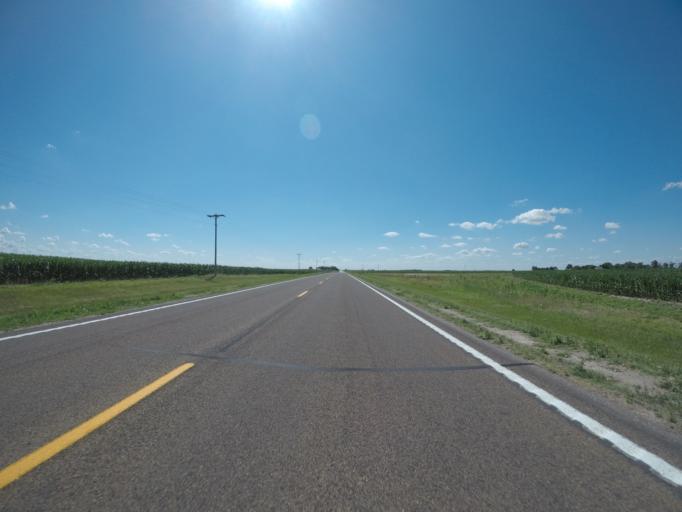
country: US
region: Nebraska
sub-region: Chase County
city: Imperial
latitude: 40.5377
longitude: -101.7195
